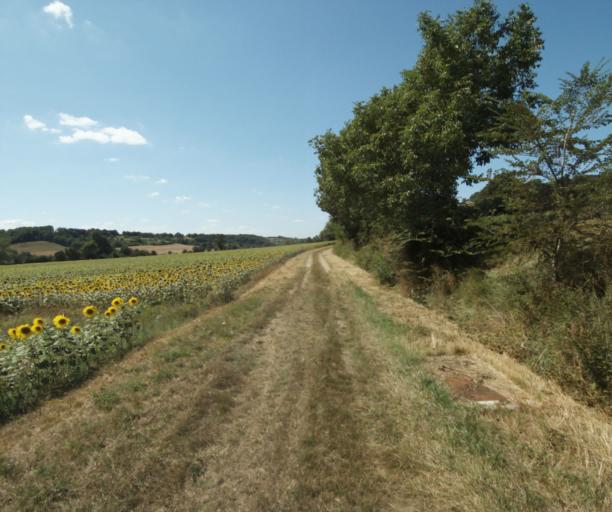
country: FR
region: Midi-Pyrenees
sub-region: Departement de la Haute-Garonne
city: Auriac-sur-Vendinelle
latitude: 43.4979
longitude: 1.8703
